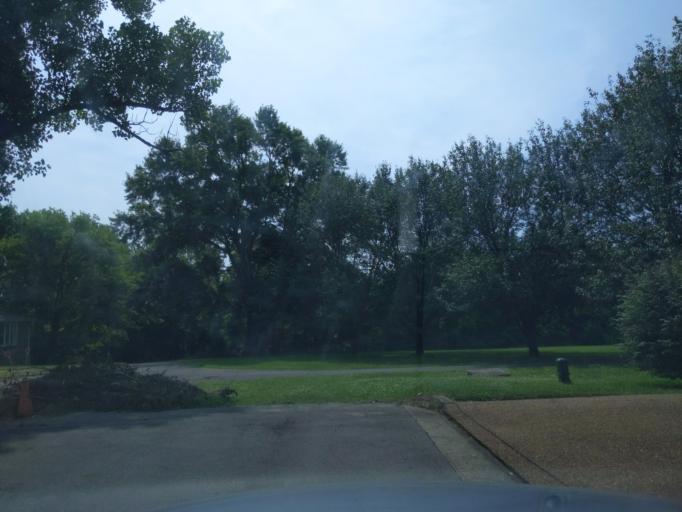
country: US
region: Tennessee
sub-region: Williamson County
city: Brentwood Estates
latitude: 36.0335
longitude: -86.7560
